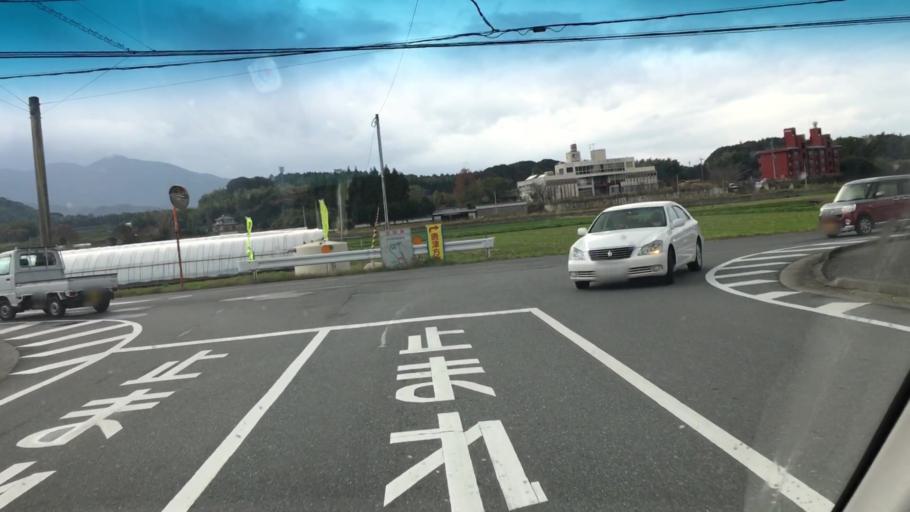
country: JP
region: Fukuoka
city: Maebaru-chuo
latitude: 33.5263
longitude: 130.1913
